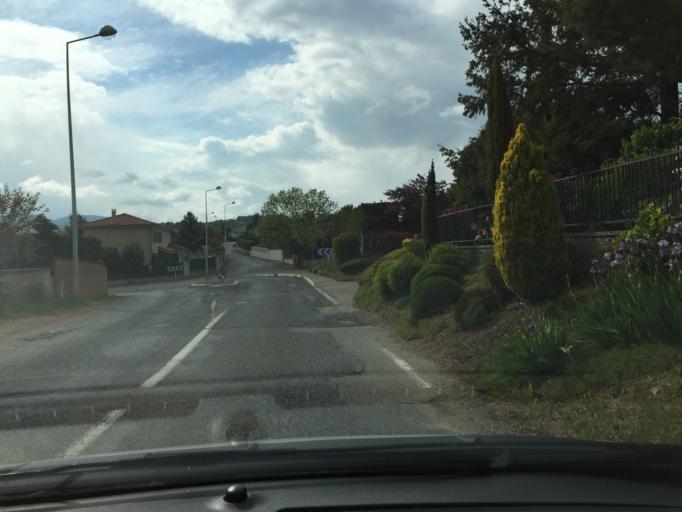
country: FR
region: Rhone-Alpes
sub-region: Departement du Rhone
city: Orlienas
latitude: 45.6452
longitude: 4.6928
